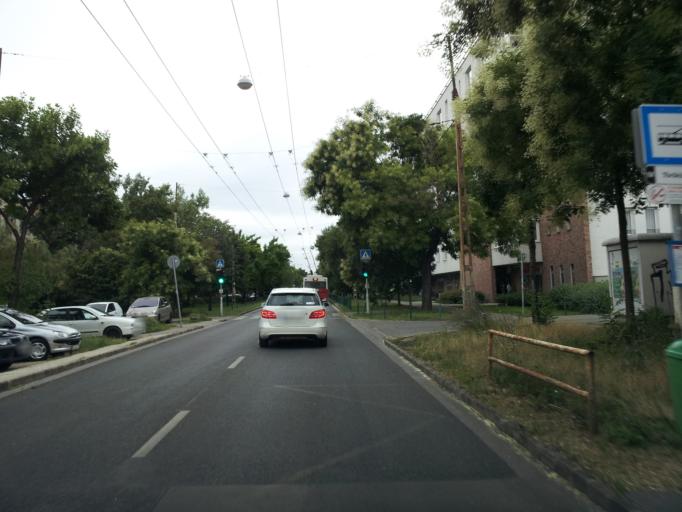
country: HU
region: Budapest
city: Budapest XIV. keruelet
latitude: 47.5082
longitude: 19.1084
